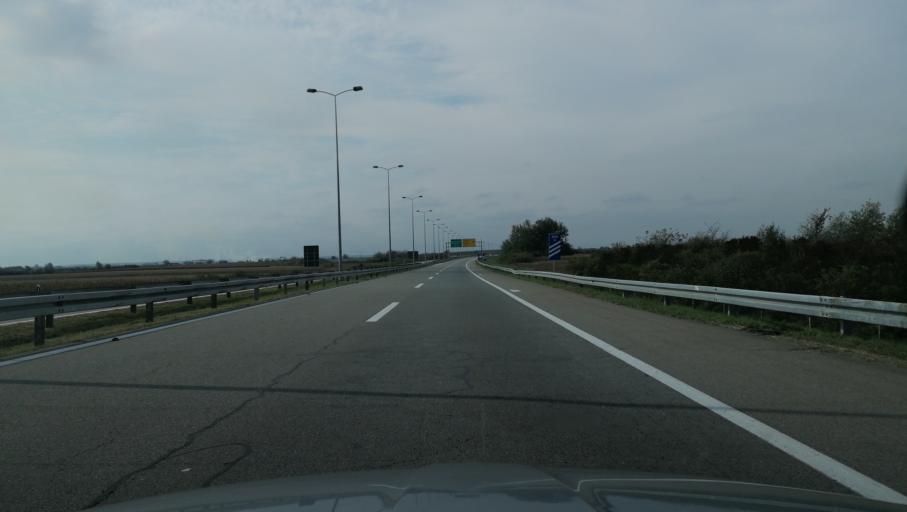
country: RS
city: Ravnje
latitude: 45.0415
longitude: 19.3983
